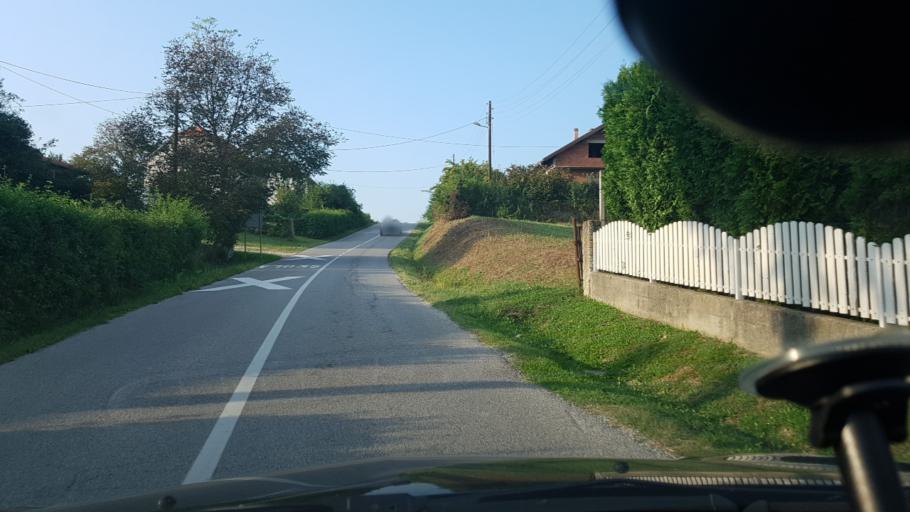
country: HR
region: Krapinsko-Zagorska
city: Zabok
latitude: 46.0223
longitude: 15.8607
